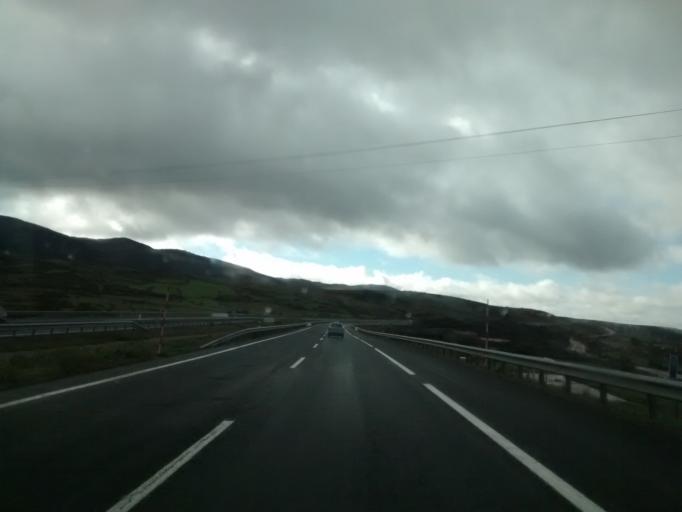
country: ES
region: Cantabria
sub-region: Provincia de Cantabria
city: Mataporquera
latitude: 42.8958
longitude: -4.1254
